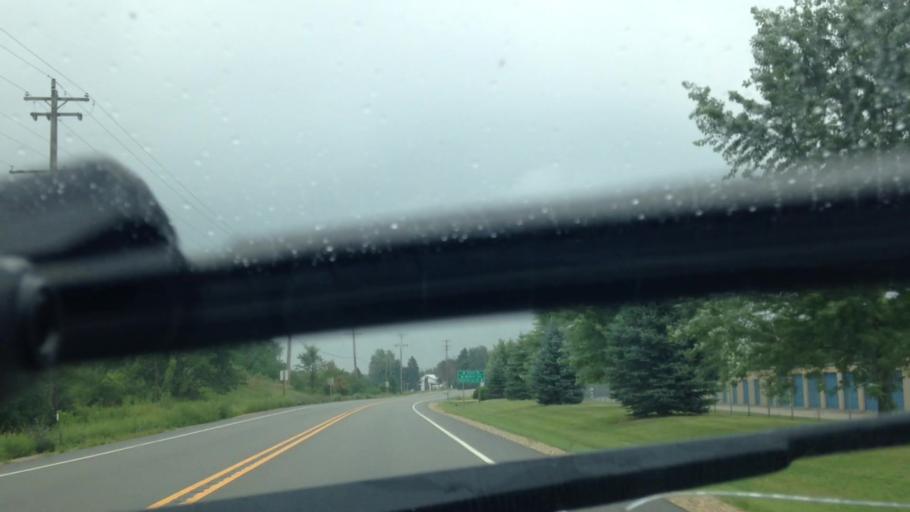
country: US
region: Wisconsin
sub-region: Washington County
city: Richfield
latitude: 43.2975
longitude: -88.2235
